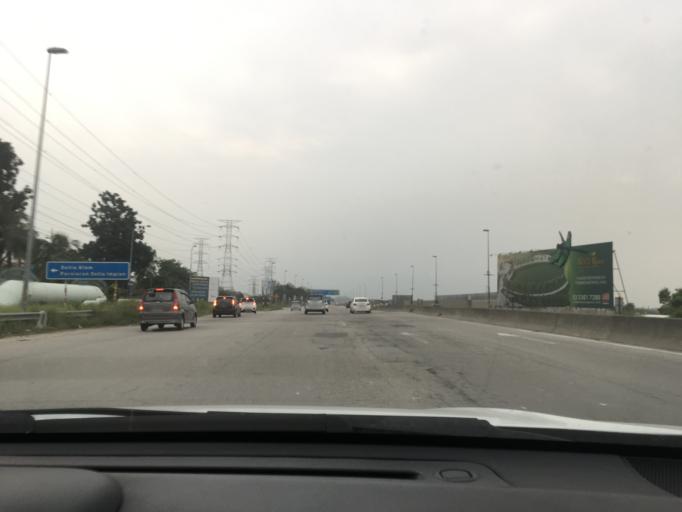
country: MY
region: Selangor
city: Klang
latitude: 3.1016
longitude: 101.4426
